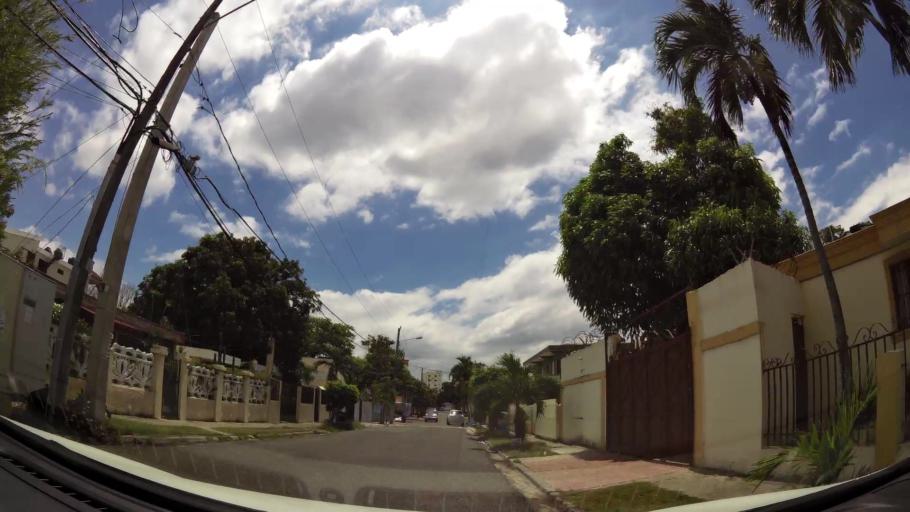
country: DO
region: Nacional
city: Bella Vista
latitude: 18.4342
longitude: -69.9589
